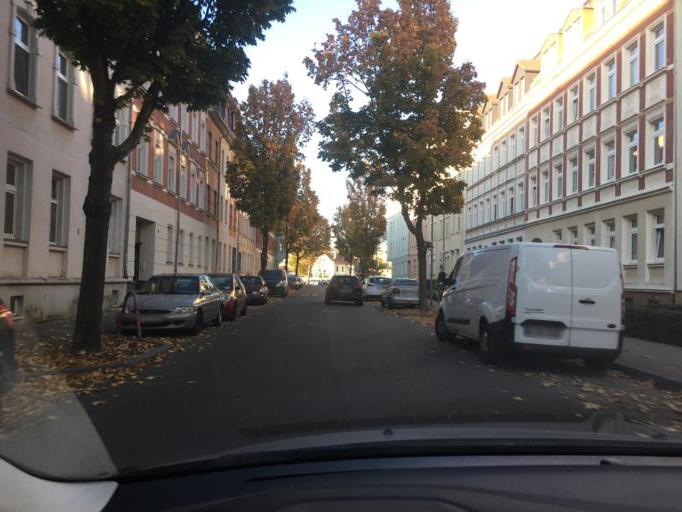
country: DE
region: Saxony
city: Markranstadt
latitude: 51.3039
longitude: 12.2257
